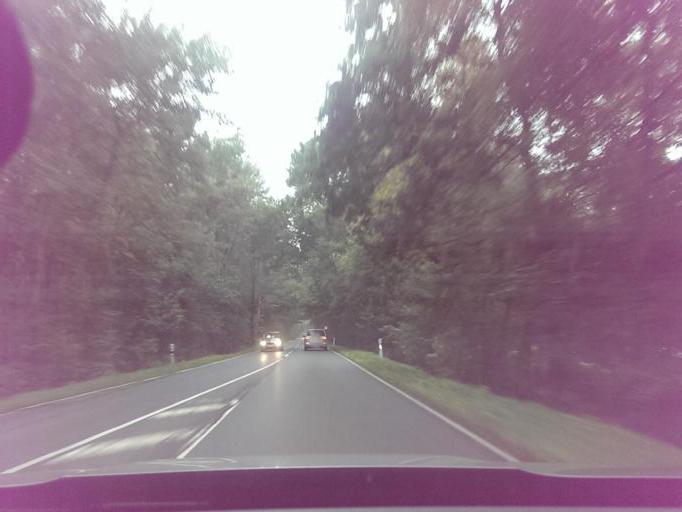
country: DE
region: Lower Saxony
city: Garbsen-Mitte
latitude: 52.4802
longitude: 9.6377
